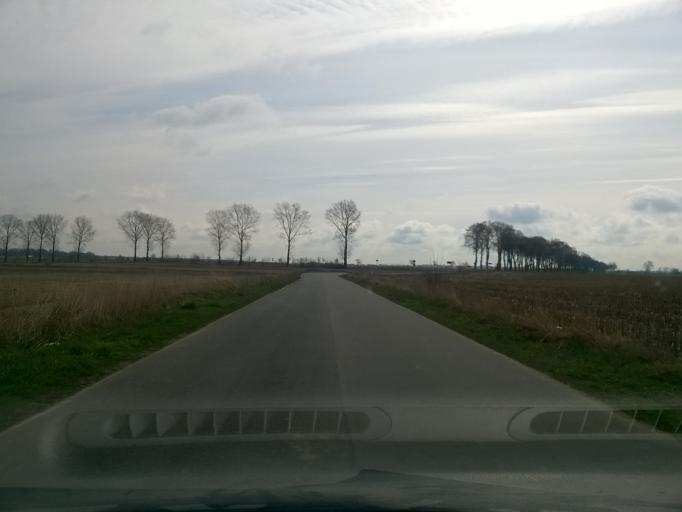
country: PL
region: Greater Poland Voivodeship
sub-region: Powiat wagrowiecki
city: Golancz
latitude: 52.9835
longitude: 17.3470
